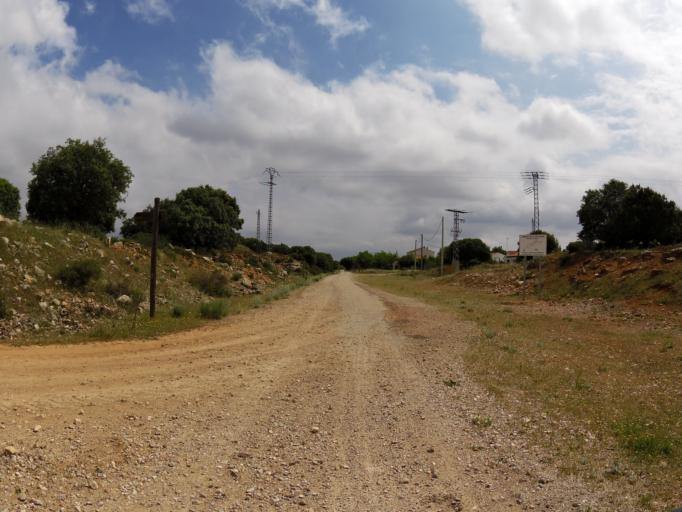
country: ES
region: Castille-La Mancha
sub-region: Provincia de Albacete
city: Robledo
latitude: 38.7689
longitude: -2.4499
